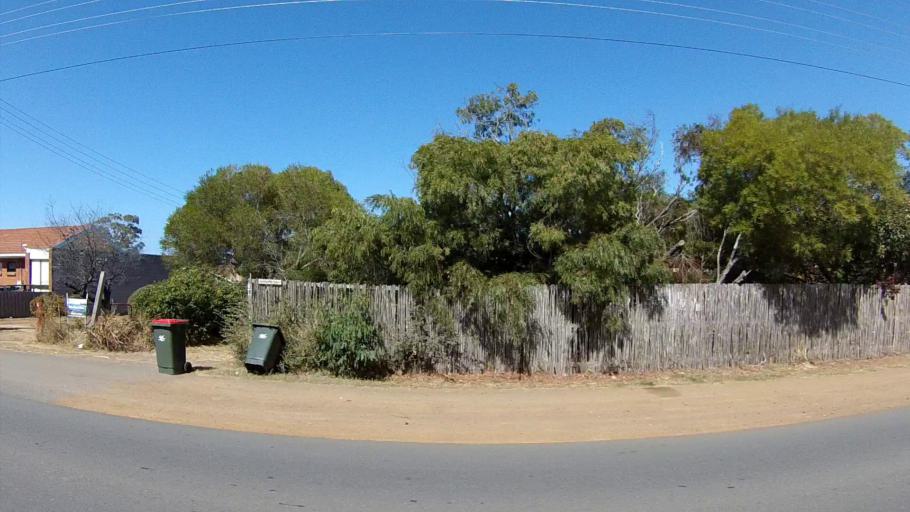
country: AU
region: Tasmania
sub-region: Sorell
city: Sorell
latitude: -42.5529
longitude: 147.8757
